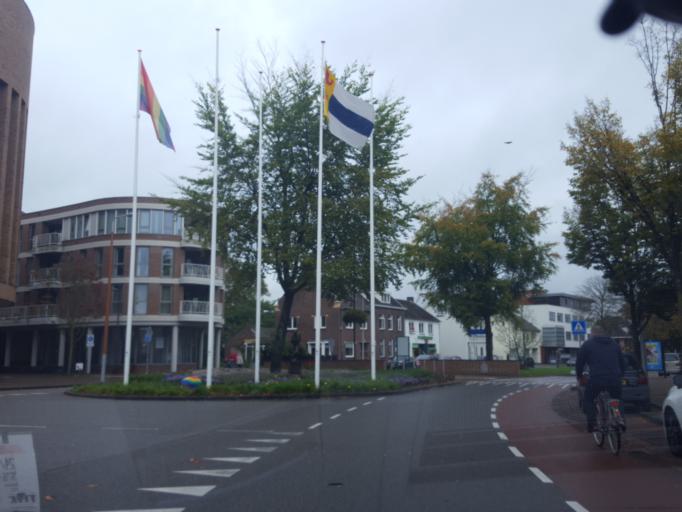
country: NL
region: Limburg
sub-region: Gemeente Weert
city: Weert
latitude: 51.2513
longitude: 5.7046
